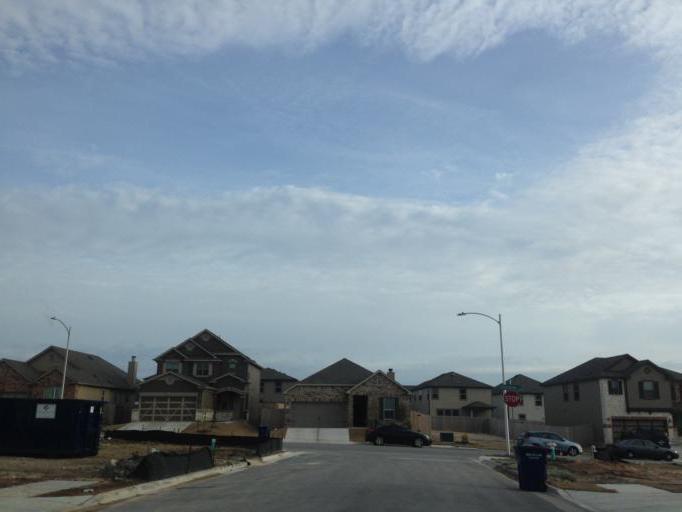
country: US
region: Texas
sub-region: Travis County
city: Wells Branch
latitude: 30.4329
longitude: -97.6568
